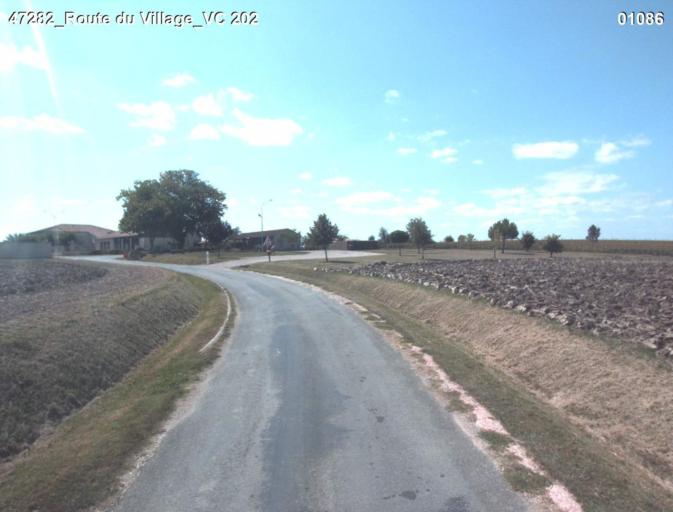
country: FR
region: Aquitaine
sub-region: Departement du Lot-et-Garonne
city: Laplume
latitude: 44.0857
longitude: 0.5126
